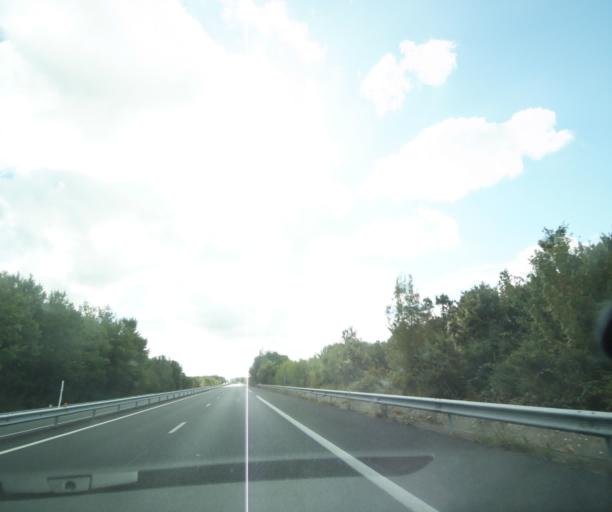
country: FR
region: Poitou-Charentes
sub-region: Departement de la Charente-Maritime
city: Bords
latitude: 45.8916
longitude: -0.7477
